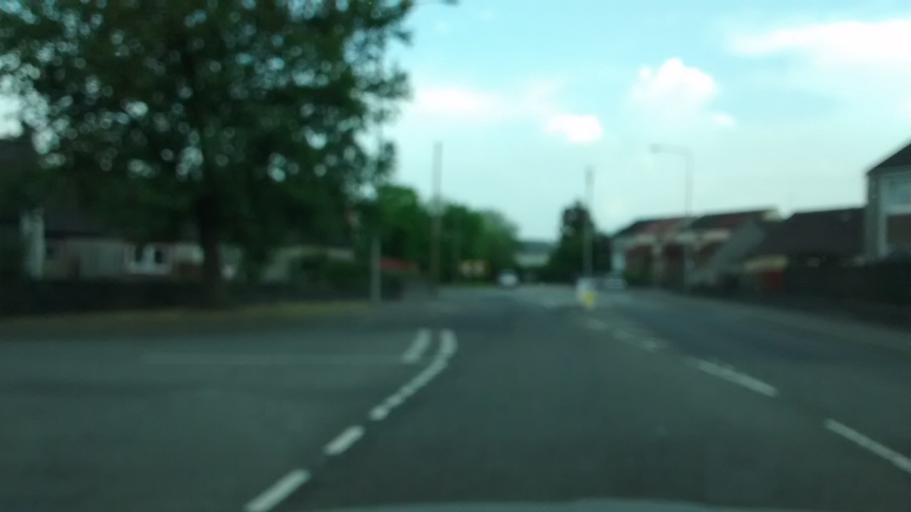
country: GB
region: Scotland
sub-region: West Lothian
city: Armadale
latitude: 55.8896
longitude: -3.7002
